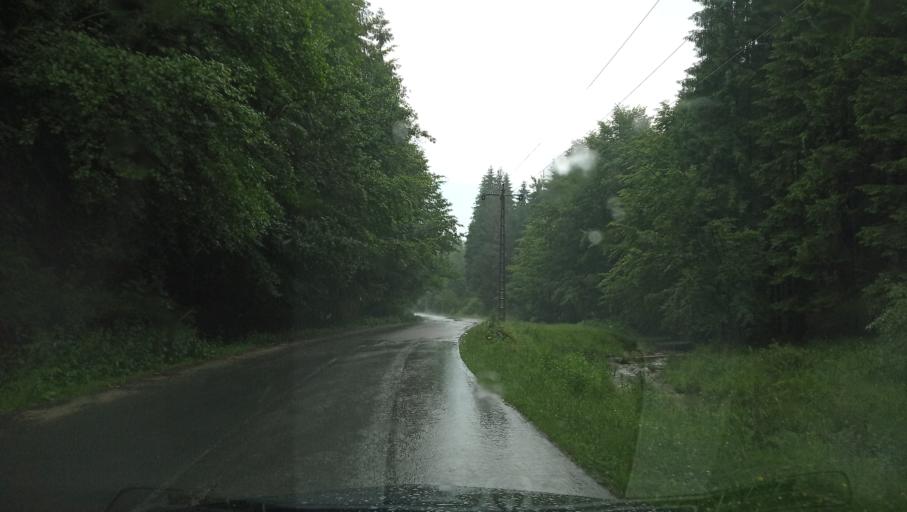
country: RO
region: Hunedoara
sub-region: Oras Petrila
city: Petrila
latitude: 45.3950
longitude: 23.4247
